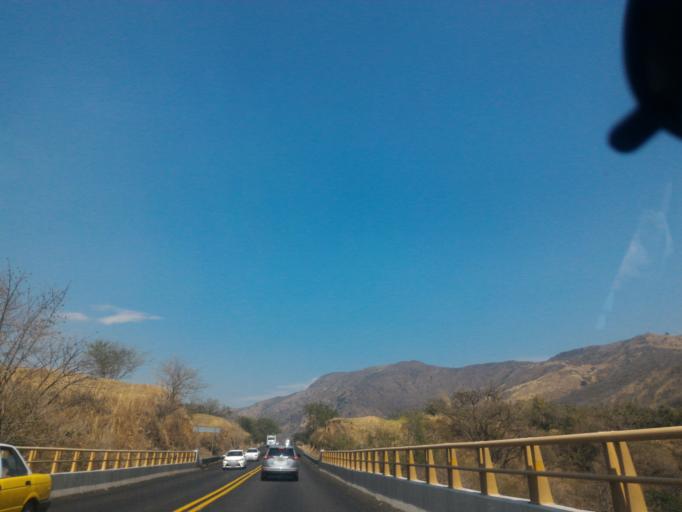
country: MX
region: Jalisco
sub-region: Tonila
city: San Marcos
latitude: 19.4814
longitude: -103.4554
